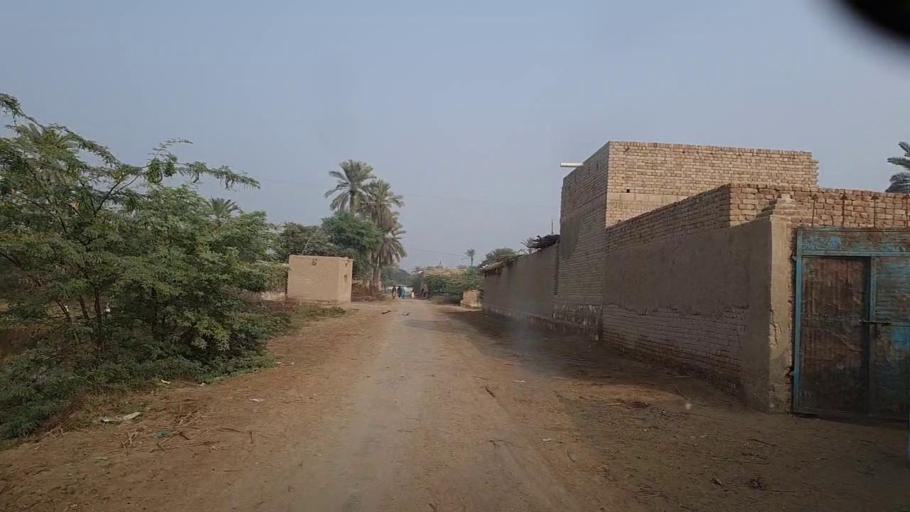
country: PK
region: Sindh
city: Bozdar
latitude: 27.1464
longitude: 68.6538
